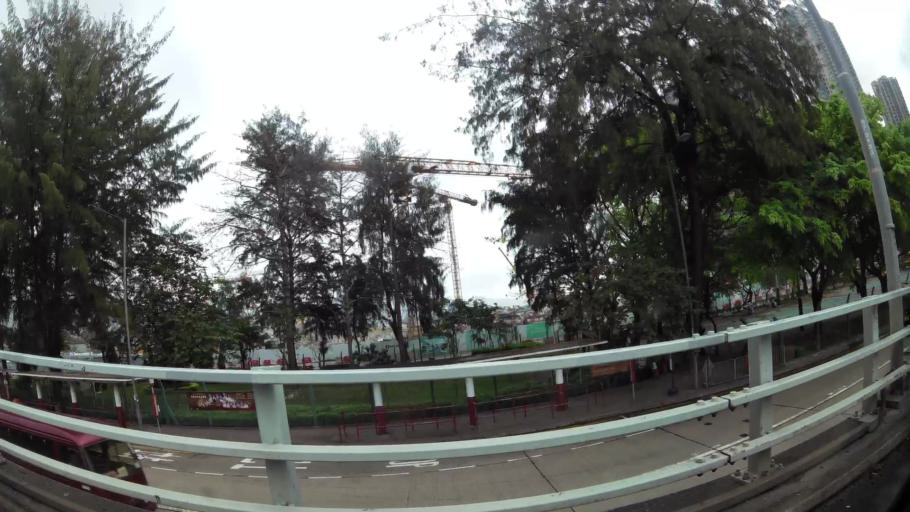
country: HK
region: Kowloon City
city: Kowloon
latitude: 22.3261
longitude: 114.1896
